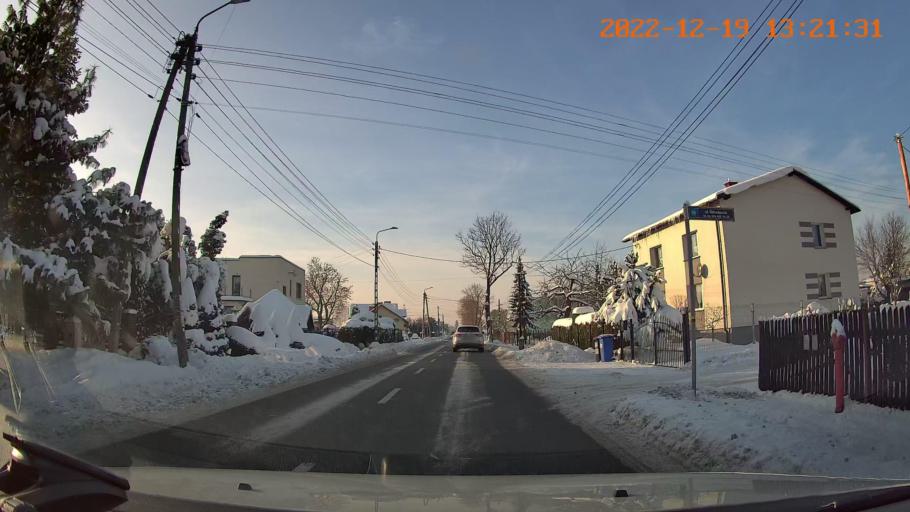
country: PL
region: Silesian Voivodeship
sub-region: Powiat bierunsko-ledzinski
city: Chelm Slaski
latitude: 50.1076
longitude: 19.1817
